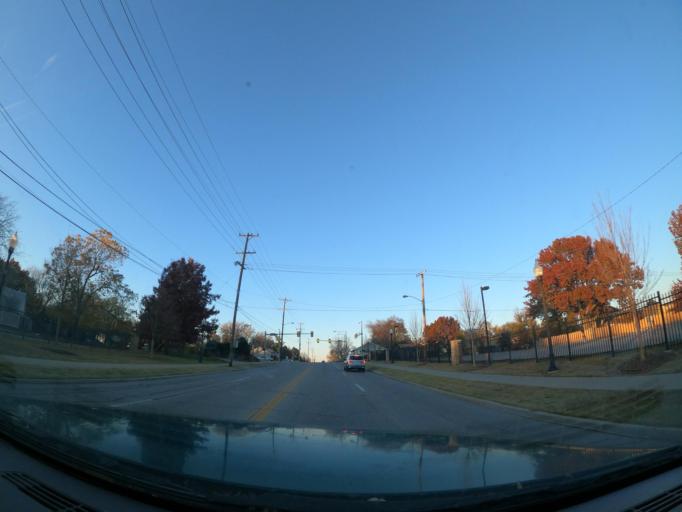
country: US
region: Oklahoma
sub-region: Tulsa County
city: Tulsa
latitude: 36.1553
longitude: -95.9403
